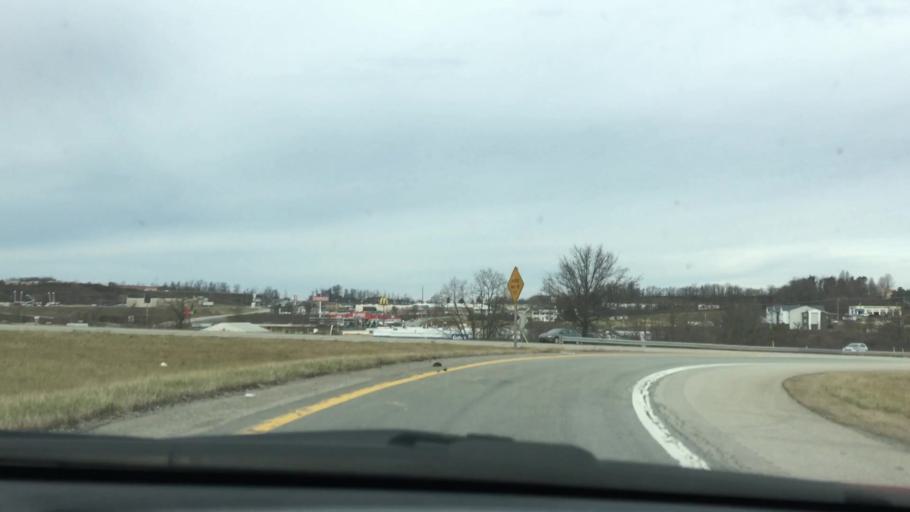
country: US
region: Pennsylvania
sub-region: Fayette County
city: South Uniontown
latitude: 39.8975
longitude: -79.7509
